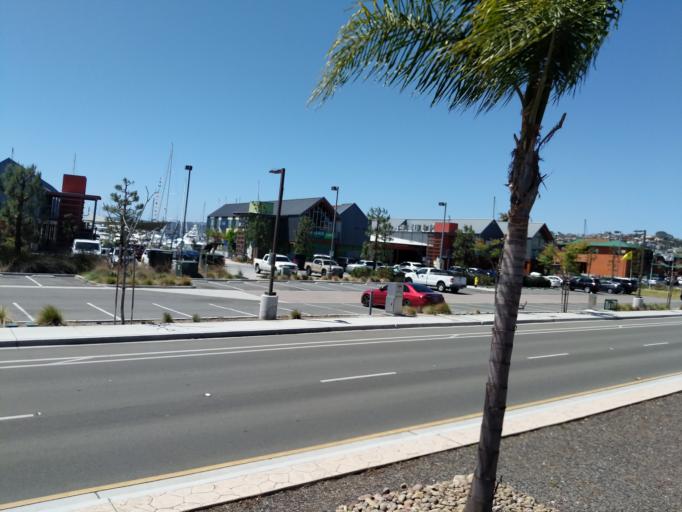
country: US
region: California
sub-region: San Diego County
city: Coronado
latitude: 32.7257
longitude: -117.2235
